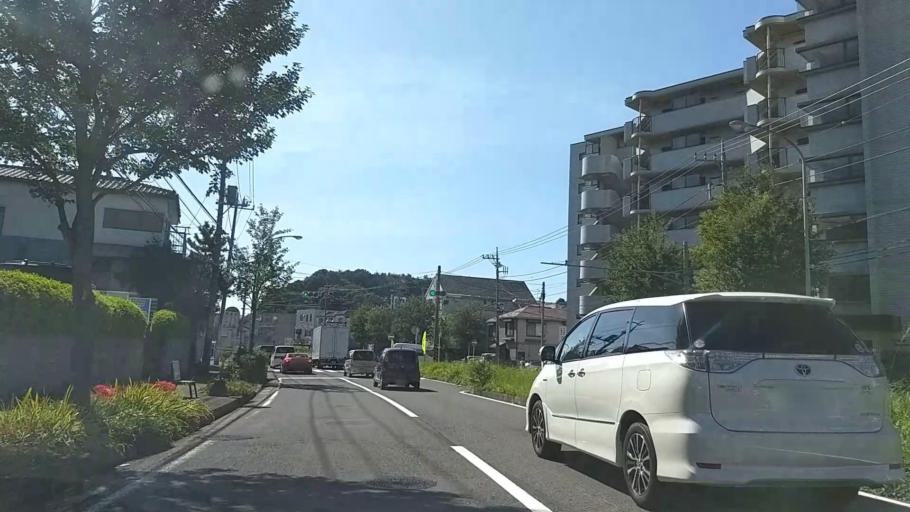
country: JP
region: Tokyo
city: Chofugaoka
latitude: 35.5836
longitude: 139.5440
